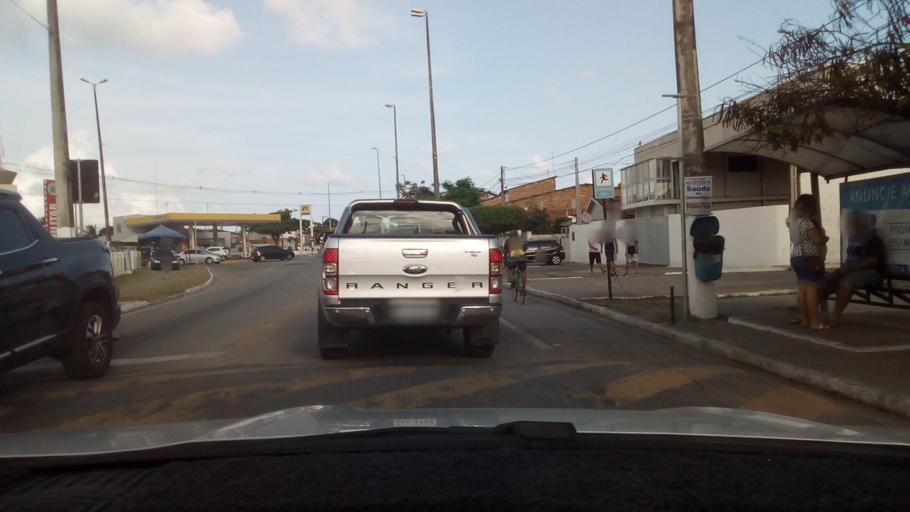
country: BR
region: Paraiba
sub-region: Cabedelo
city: Cabedelo
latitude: -6.9719
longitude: -34.8344
